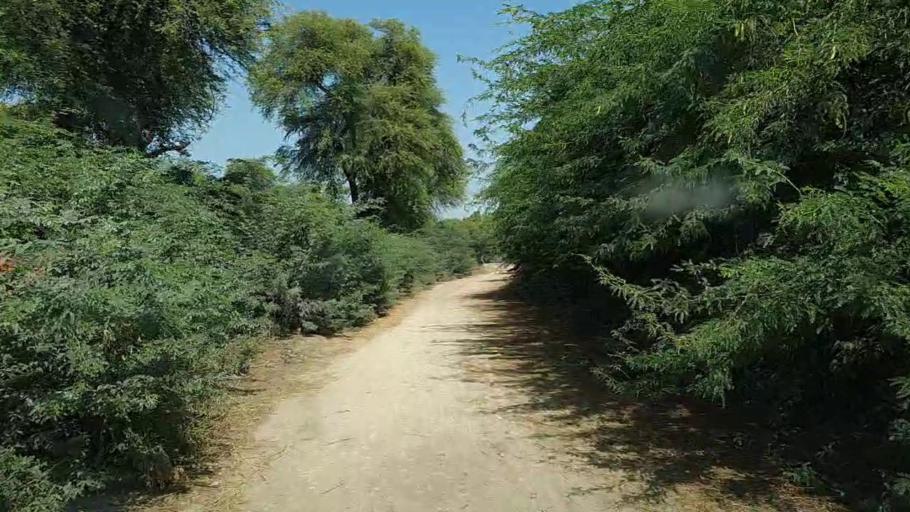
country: PK
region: Sindh
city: Mirpur Batoro
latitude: 24.7120
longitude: 68.4241
